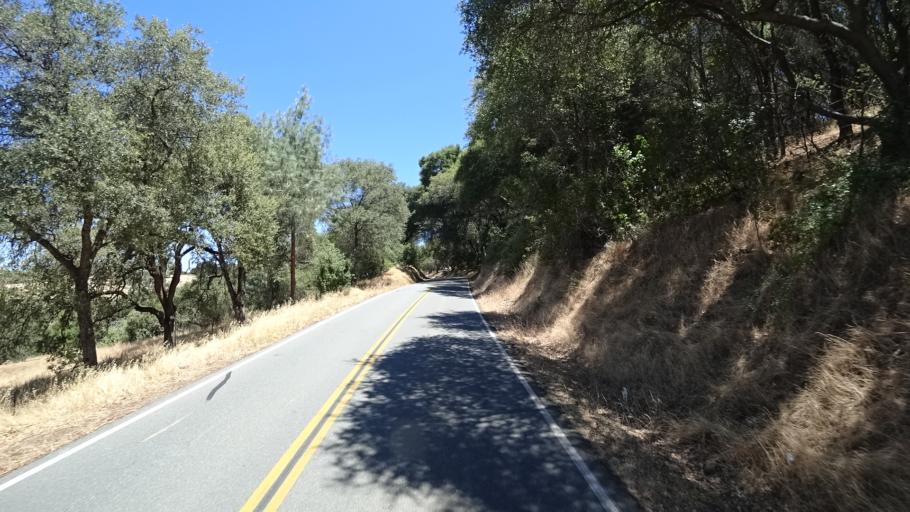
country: US
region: California
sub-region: Amador County
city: Jackson
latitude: 38.2583
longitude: -120.7588
